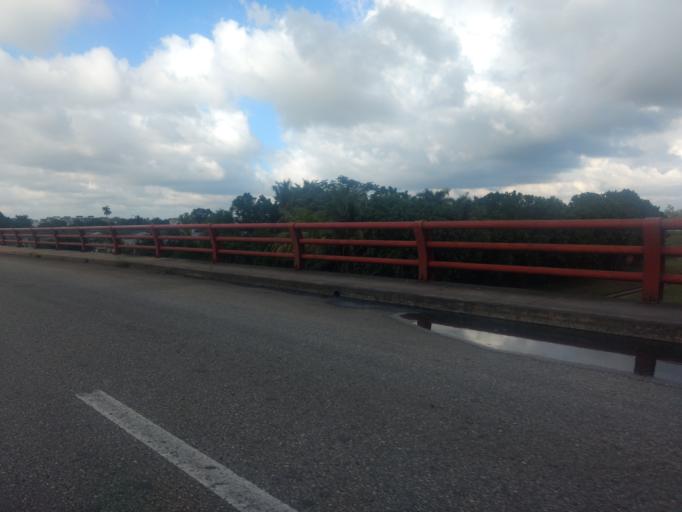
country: CU
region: La Habana
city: Boyeros
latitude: 22.9999
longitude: -82.4131
